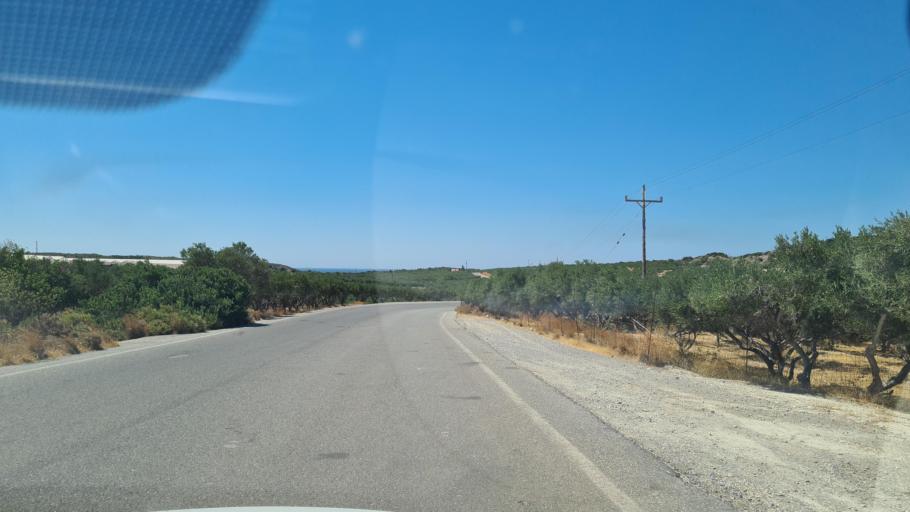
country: GR
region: Crete
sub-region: Nomos Chanias
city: Palaiochora
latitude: 35.2945
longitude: 23.5428
